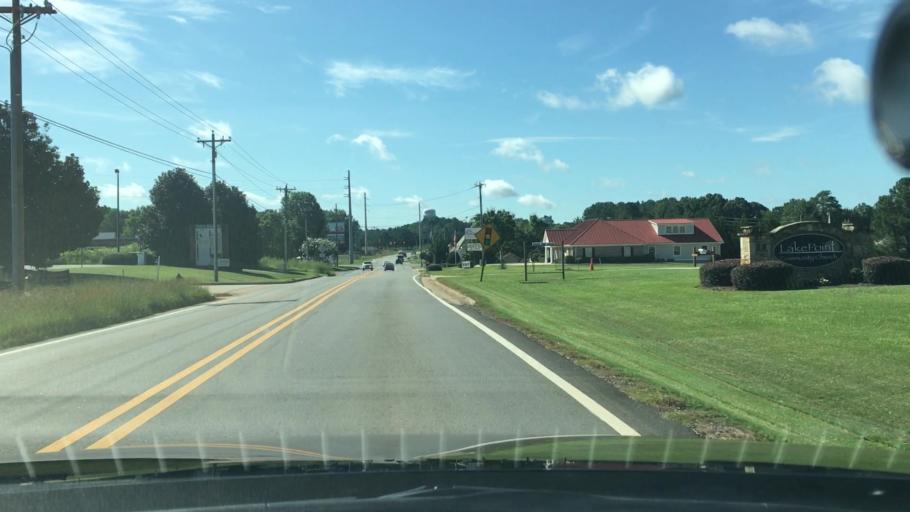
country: US
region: Georgia
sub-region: Putnam County
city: Jefferson
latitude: 33.4233
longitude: -83.2702
